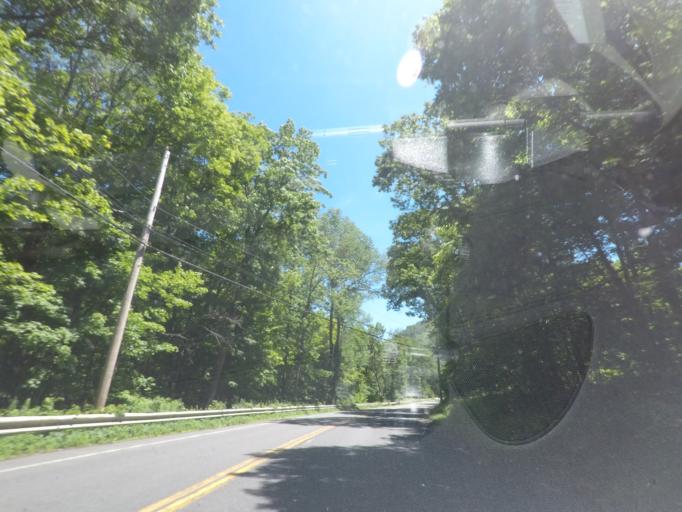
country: US
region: Massachusetts
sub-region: Berkshire County
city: Becket
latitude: 42.2580
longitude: -72.9525
